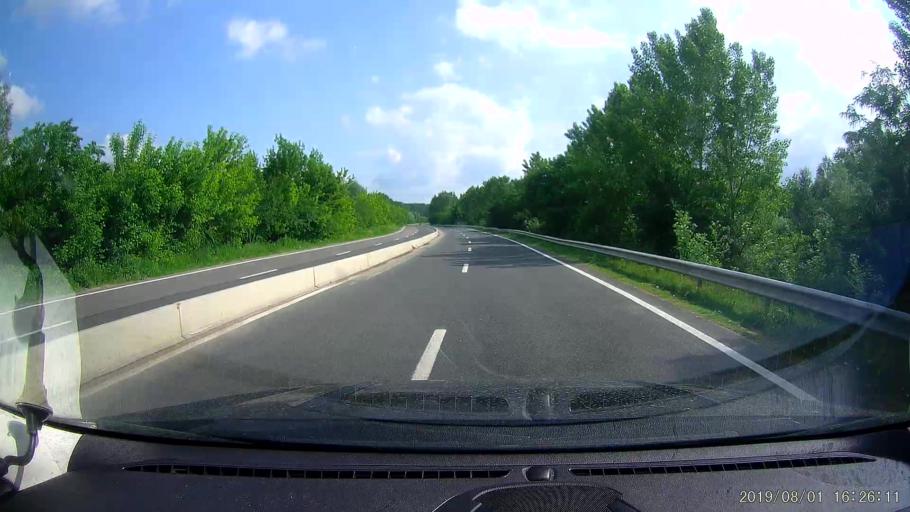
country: RO
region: Calarasi
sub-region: Municipiul Calarasi
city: Calarasi
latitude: 44.1852
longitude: 27.3217
